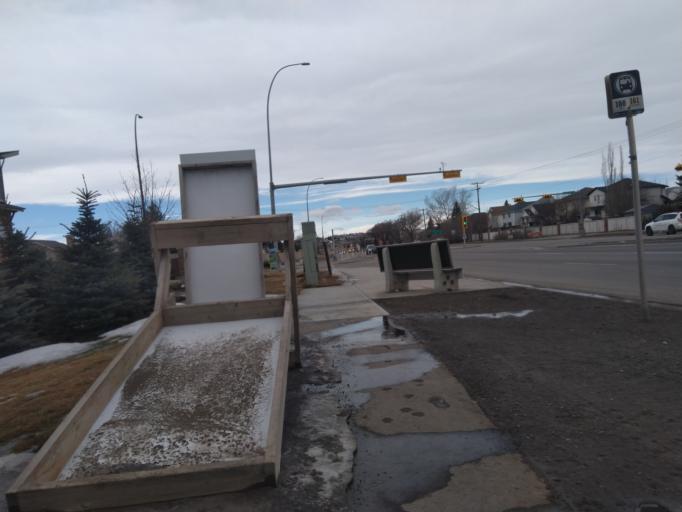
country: CA
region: Alberta
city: Calgary
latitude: 51.1541
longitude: -114.0473
